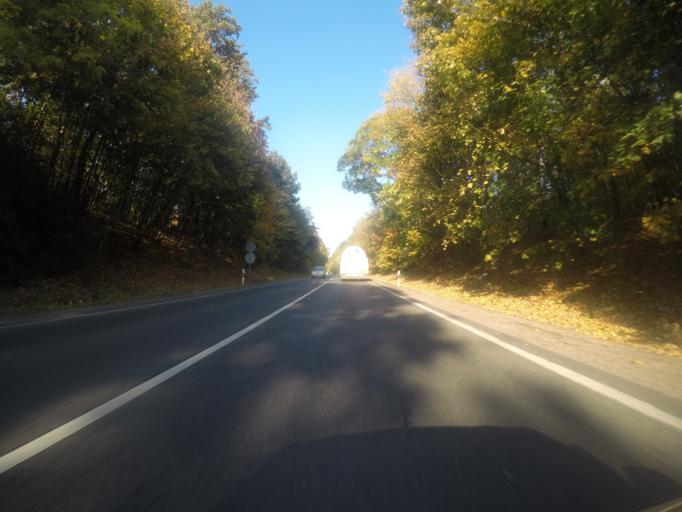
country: HU
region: Fejer
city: dunaujvaros
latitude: 46.9747
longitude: 18.9097
